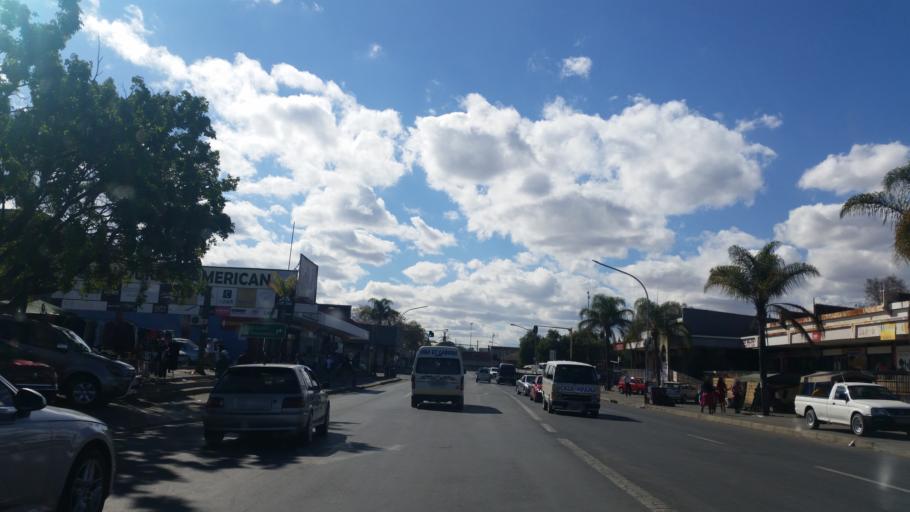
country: ZA
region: KwaZulu-Natal
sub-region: uThukela District Municipality
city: Ladysmith
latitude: -28.5592
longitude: 29.7839
